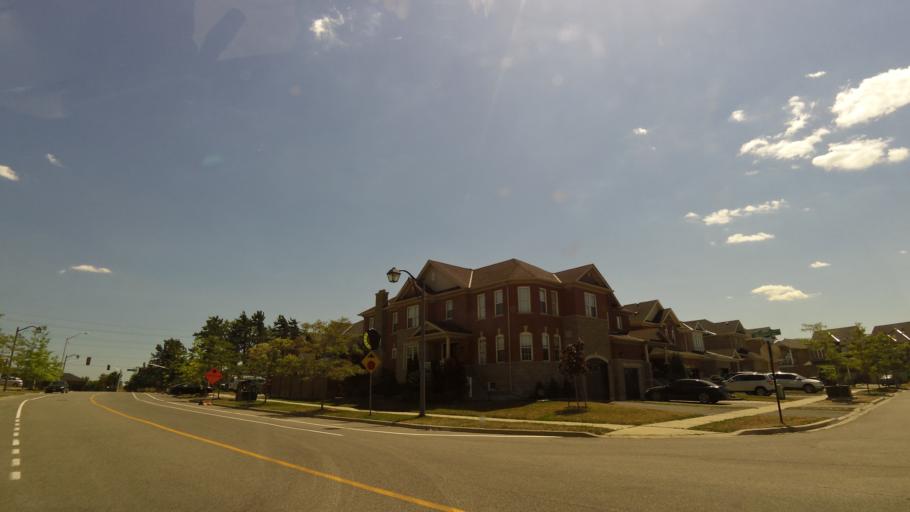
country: CA
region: Ontario
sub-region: Halton
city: Milton
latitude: 43.6319
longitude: -79.8707
